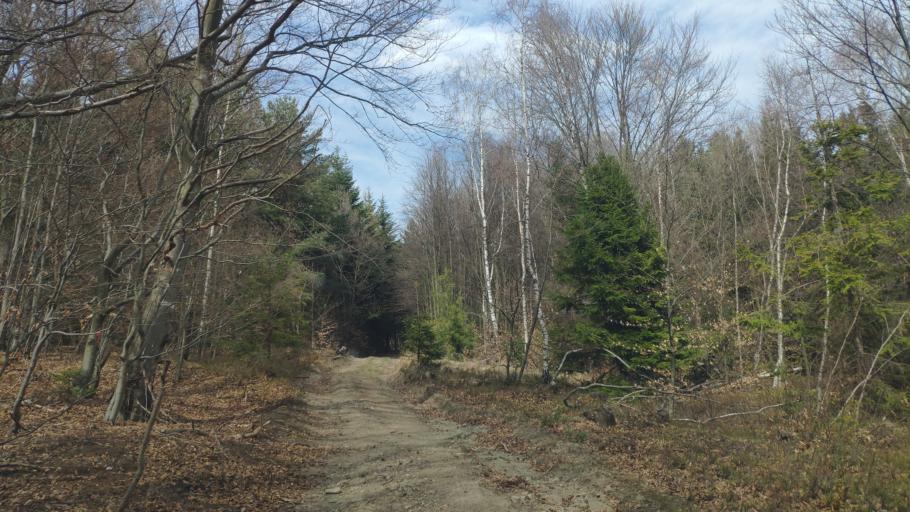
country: SK
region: Kosicky
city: Gelnica
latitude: 48.7532
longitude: 21.0207
